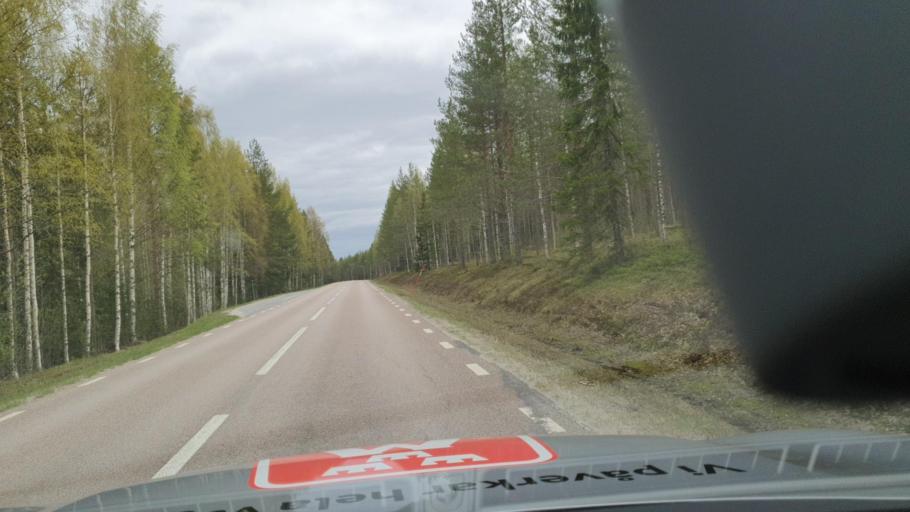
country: SE
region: Vaesternorrland
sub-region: OErnskoeldsviks Kommun
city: Ornskoldsvik
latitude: 63.4928
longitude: 18.8727
